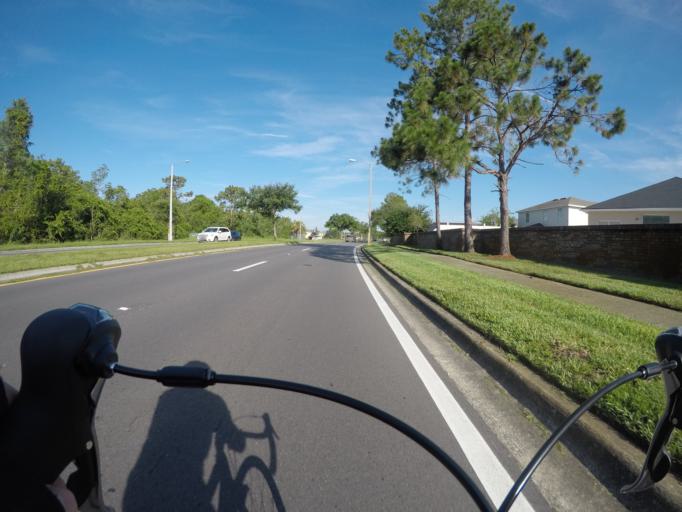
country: US
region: Florida
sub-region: Osceola County
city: Buenaventura Lakes
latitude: 28.3600
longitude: -81.3541
